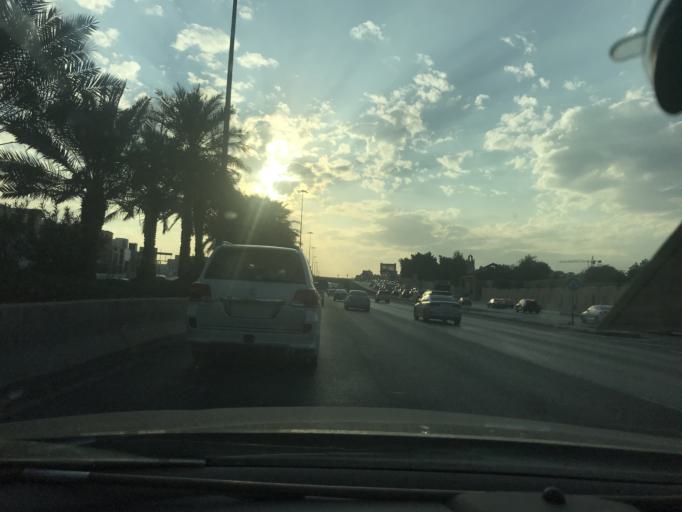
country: SA
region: Ar Riyad
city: Riyadh
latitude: 24.7498
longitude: 46.6203
